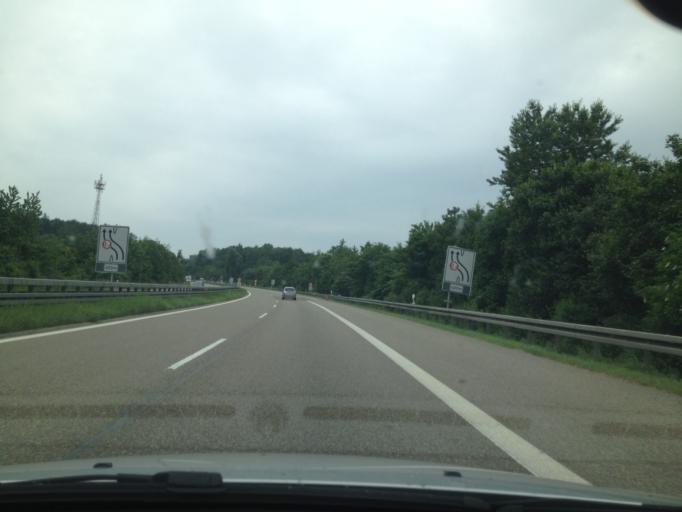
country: DE
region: Baden-Wuerttemberg
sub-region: Regierungsbezirk Stuttgart
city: Giengen an der Brenz
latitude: 48.6562
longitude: 10.2325
